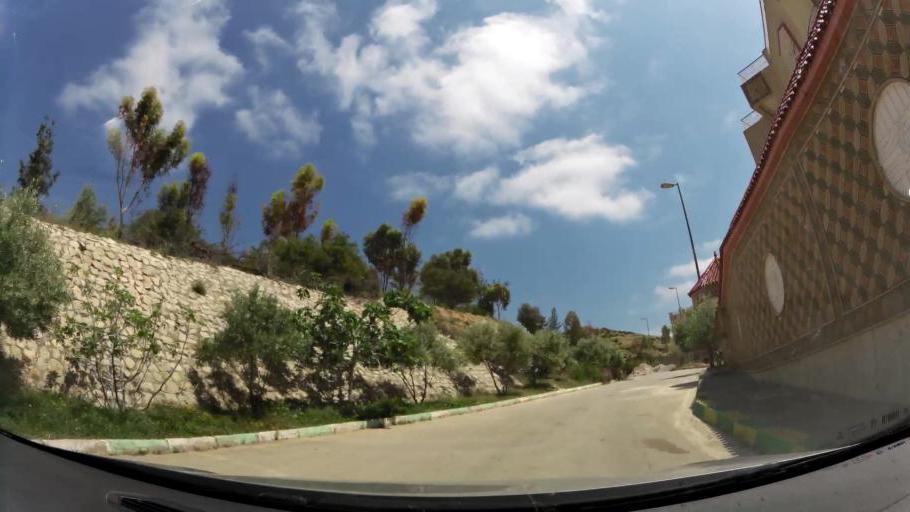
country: MA
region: Fes-Boulemane
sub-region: Fes
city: Fes
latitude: 34.0633
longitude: -5.0248
